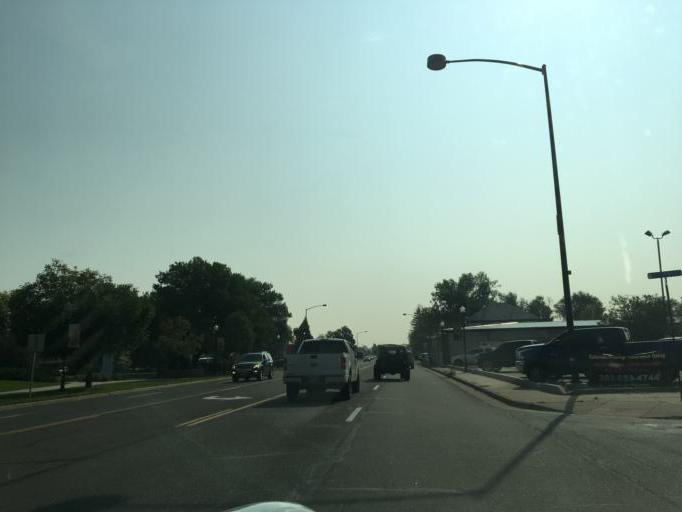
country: US
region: Colorado
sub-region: Adams County
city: Brighton
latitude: 39.9867
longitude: -104.8172
